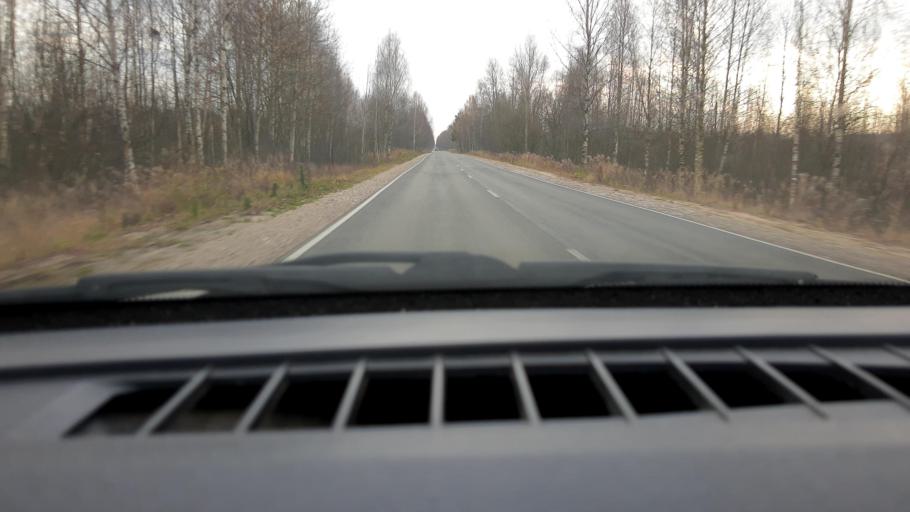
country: RU
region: Nizjnij Novgorod
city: Neklyudovo
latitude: 56.4912
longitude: 43.8601
